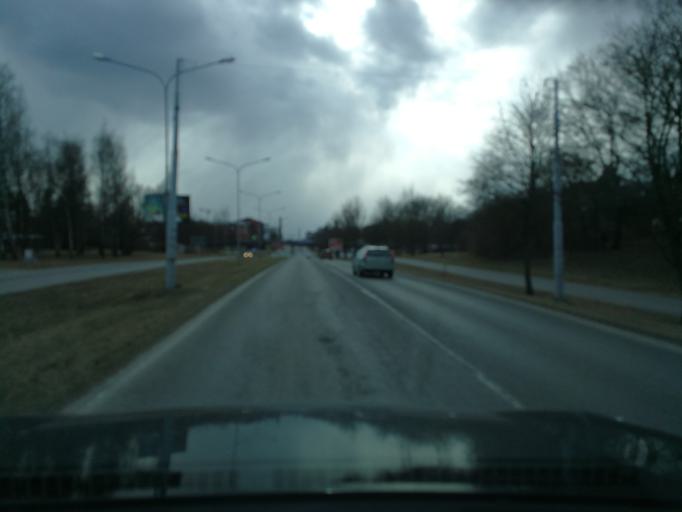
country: FI
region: Varsinais-Suomi
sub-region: Turku
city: Turku
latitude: 60.4581
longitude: 22.3069
